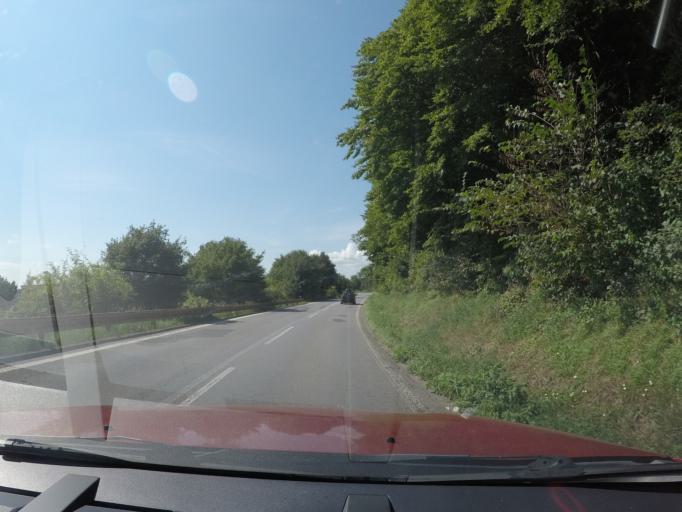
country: SK
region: Presovsky
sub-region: Okres Presov
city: Presov
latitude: 48.9429
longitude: 21.2406
